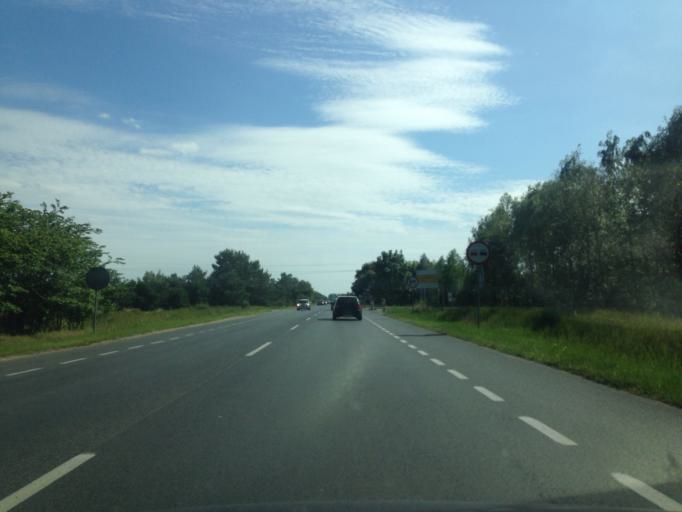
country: PL
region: Kujawsko-Pomorskie
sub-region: Powiat torunski
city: Lysomice
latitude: 53.0526
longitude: 18.6172
